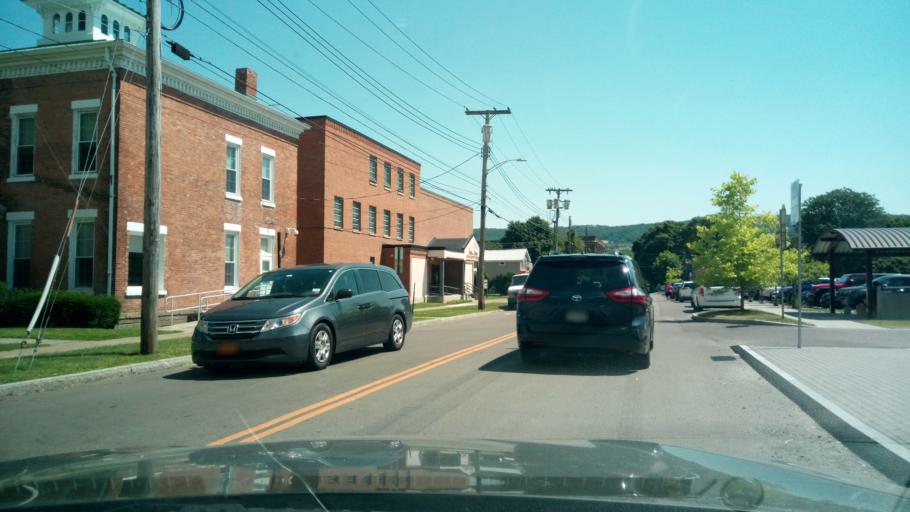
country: US
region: New York
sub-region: Schuyler County
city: Watkins Glen
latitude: 42.3763
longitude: -76.8711
